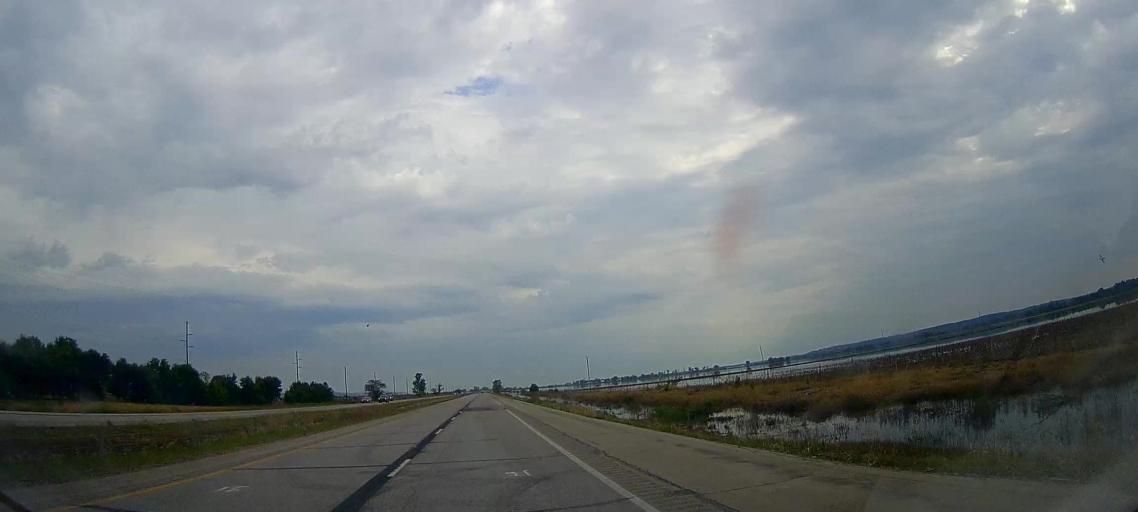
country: US
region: Iowa
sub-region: Harrison County
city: Missouri Valley
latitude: 41.4505
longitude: -95.8998
